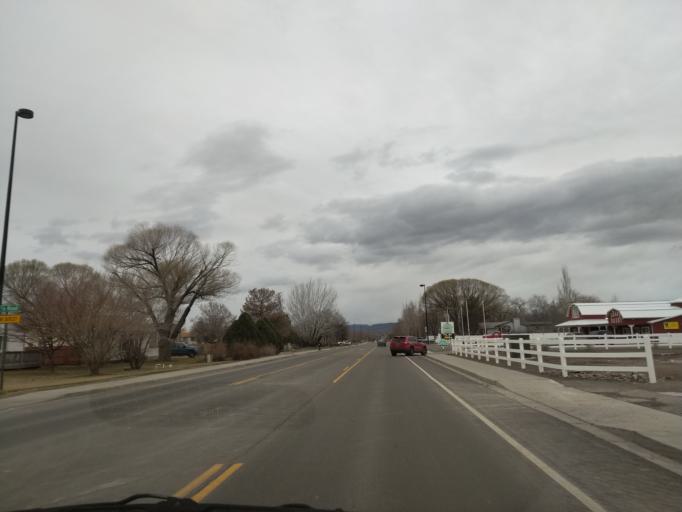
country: US
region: Colorado
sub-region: Mesa County
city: Fruitvale
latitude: 39.0893
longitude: -108.5152
